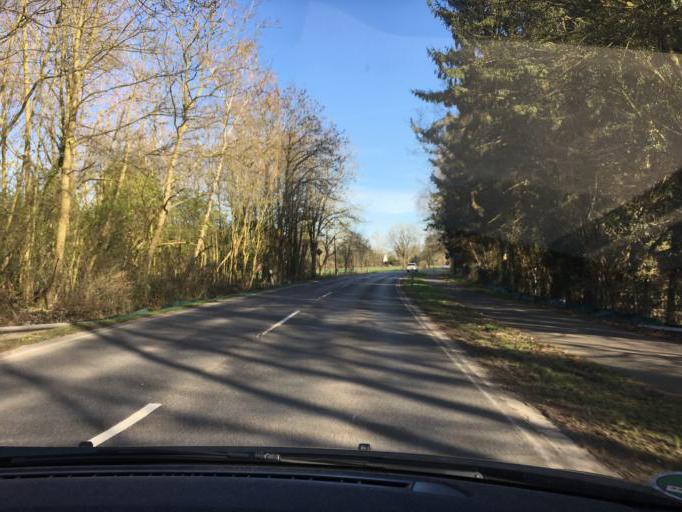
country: DE
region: North Rhine-Westphalia
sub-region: Regierungsbezirk Dusseldorf
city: Korschenbroich
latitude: 51.1945
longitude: 6.5330
